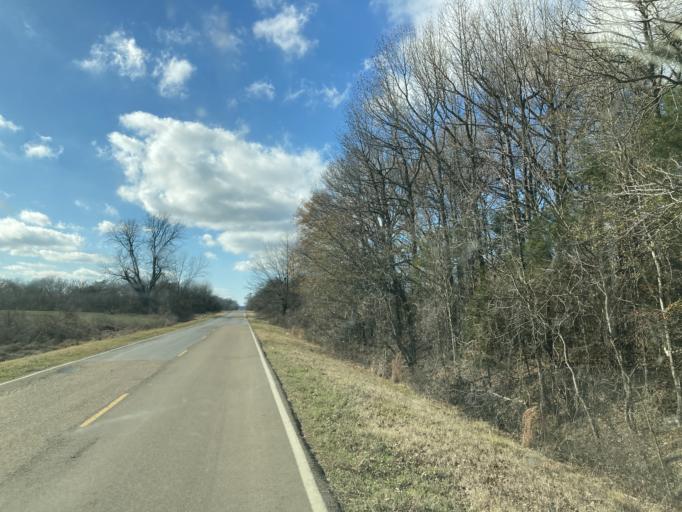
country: US
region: Mississippi
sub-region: Yazoo County
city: Yazoo City
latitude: 32.9652
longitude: -90.4648
